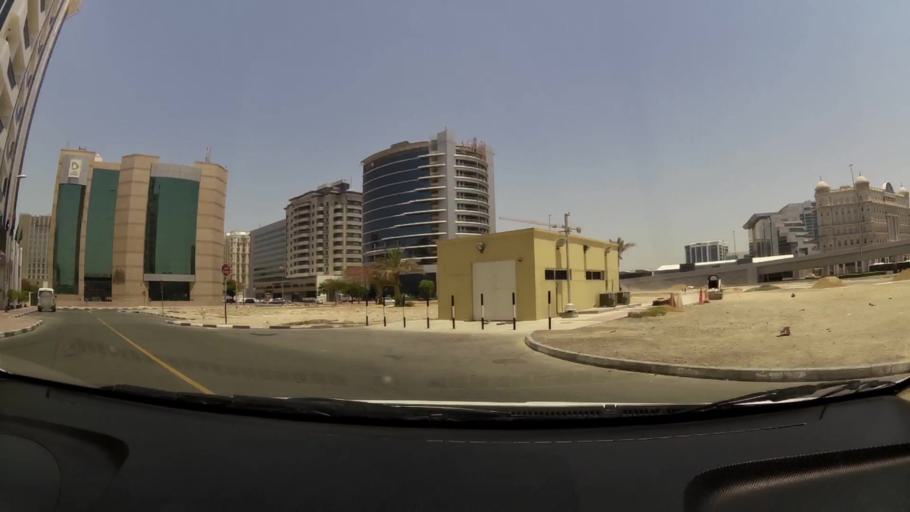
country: AE
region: Ash Shariqah
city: Sharjah
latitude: 25.2552
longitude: 55.3356
